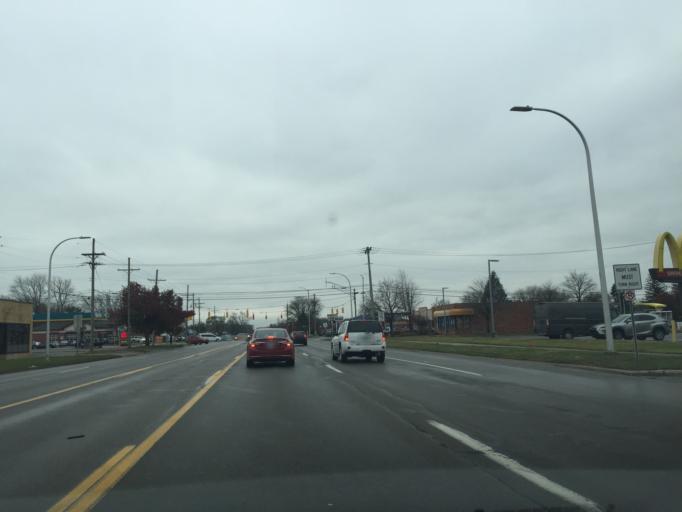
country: US
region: Michigan
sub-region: Wayne County
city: Livonia
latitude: 42.3994
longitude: -83.3346
